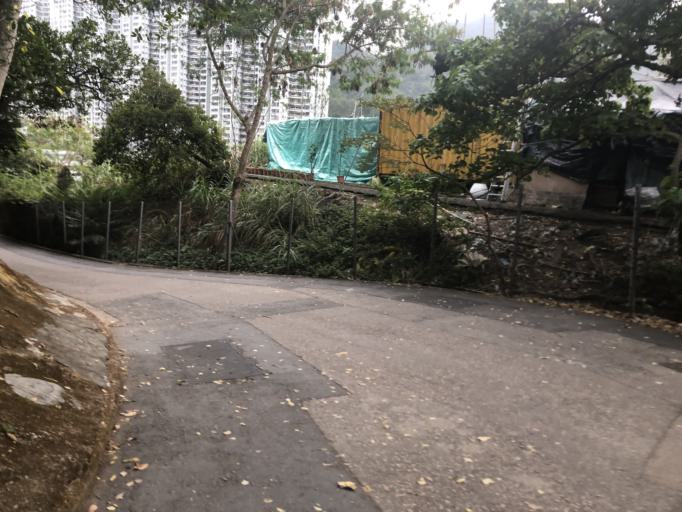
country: HK
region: Wanchai
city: Wan Chai
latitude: 22.2809
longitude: 114.2114
